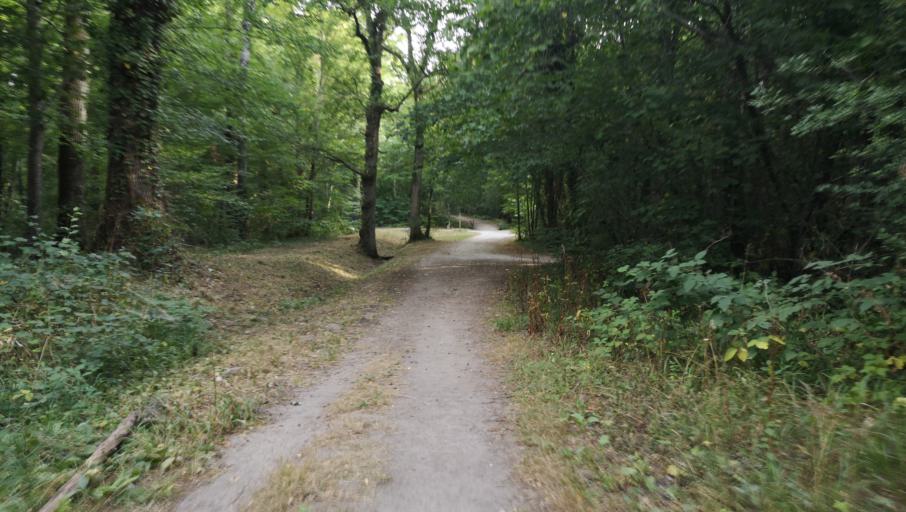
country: FR
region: Centre
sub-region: Departement du Loiret
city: Boigny-sur-Bionne
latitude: 47.9419
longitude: 1.9940
